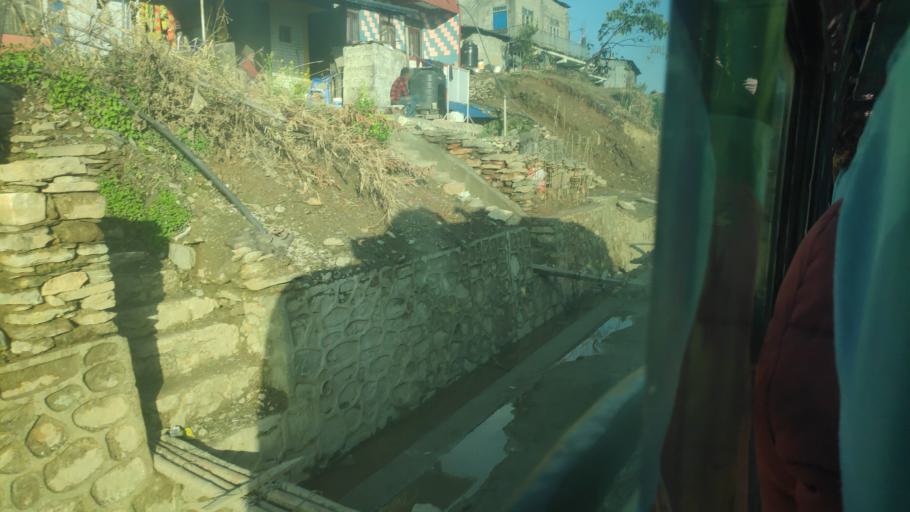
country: NP
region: Western Region
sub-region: Gandaki Zone
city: Pokhara
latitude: 28.2815
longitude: 83.8627
